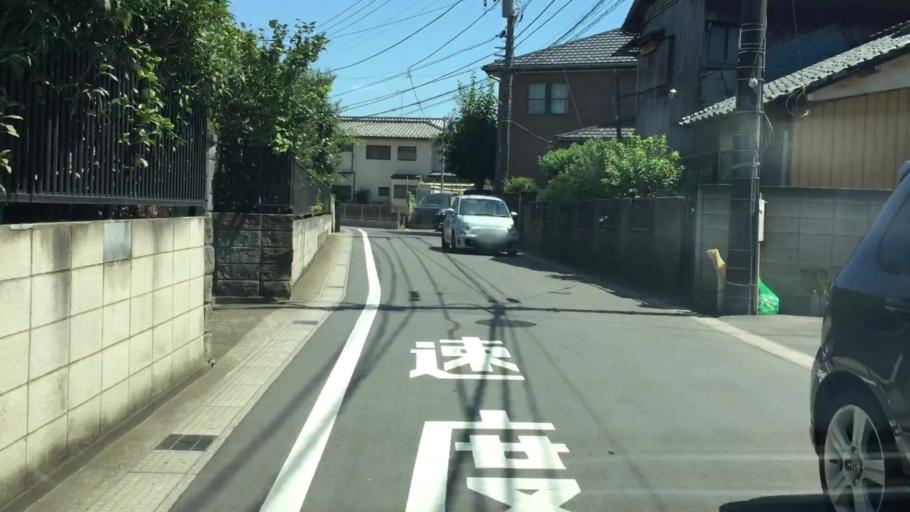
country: JP
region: Chiba
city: Funabashi
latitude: 35.7347
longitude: 139.9772
